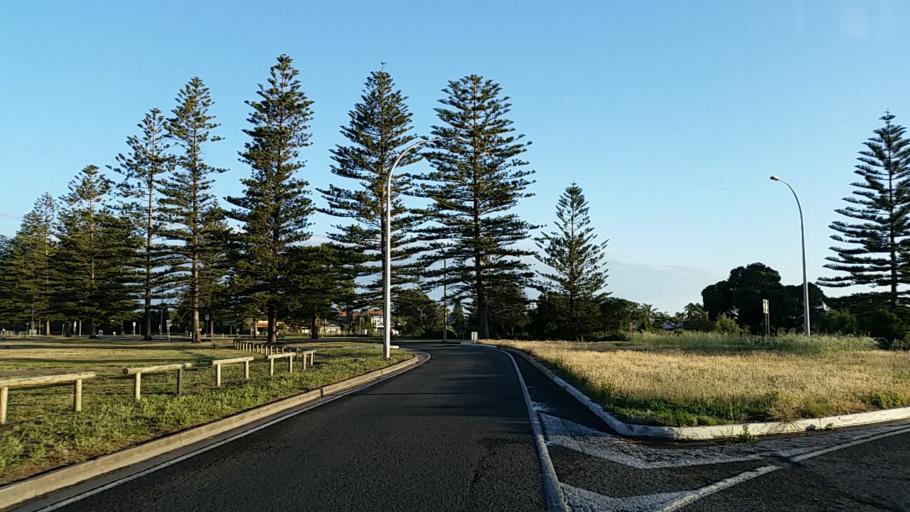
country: AU
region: South Australia
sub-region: Port Adelaide Enfield
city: Birkenhead
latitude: -34.7803
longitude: 138.4829
